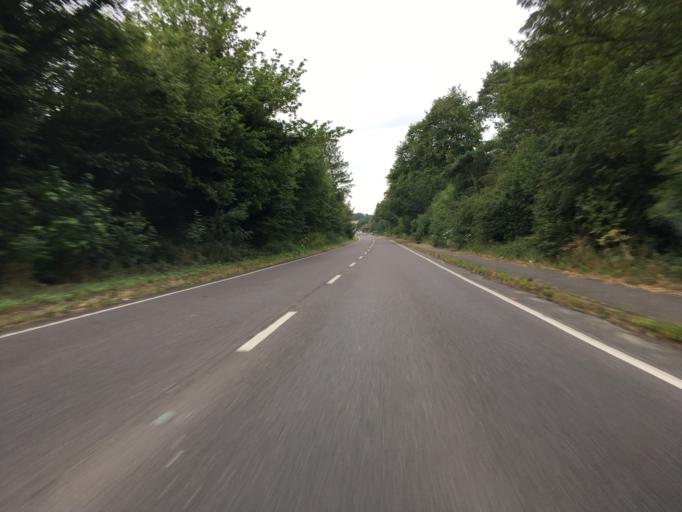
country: GB
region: England
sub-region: Hertfordshire
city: Markyate
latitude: 51.8438
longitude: -0.4691
